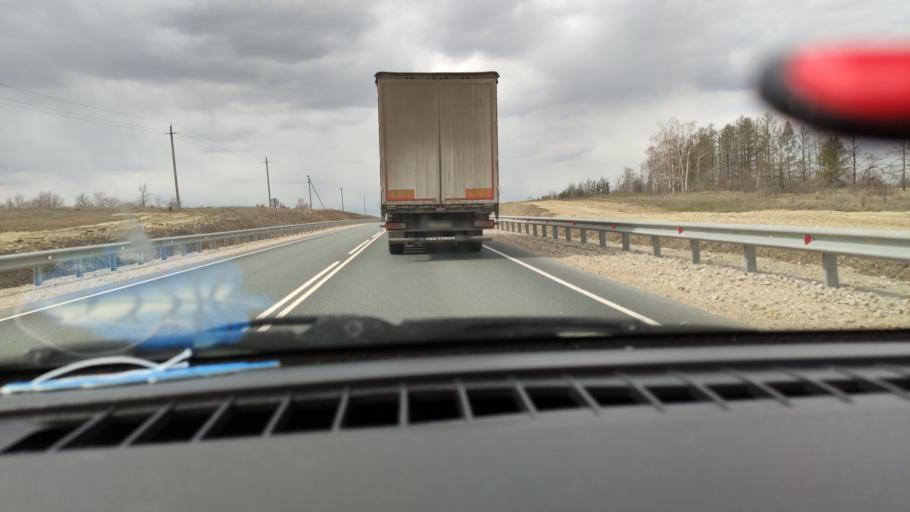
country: RU
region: Saratov
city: Shikhany
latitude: 52.1615
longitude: 47.1098
